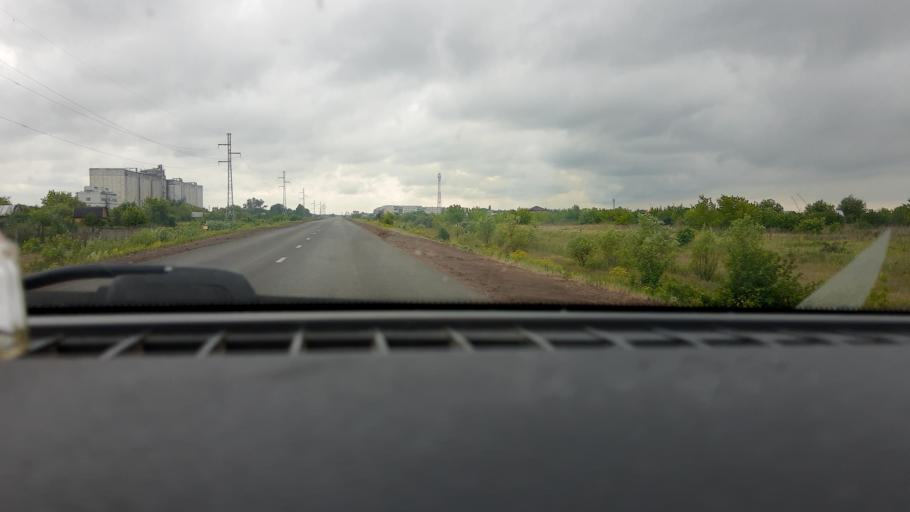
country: RU
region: Bashkortostan
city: Priyutovo
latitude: 53.9127
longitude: 53.9494
